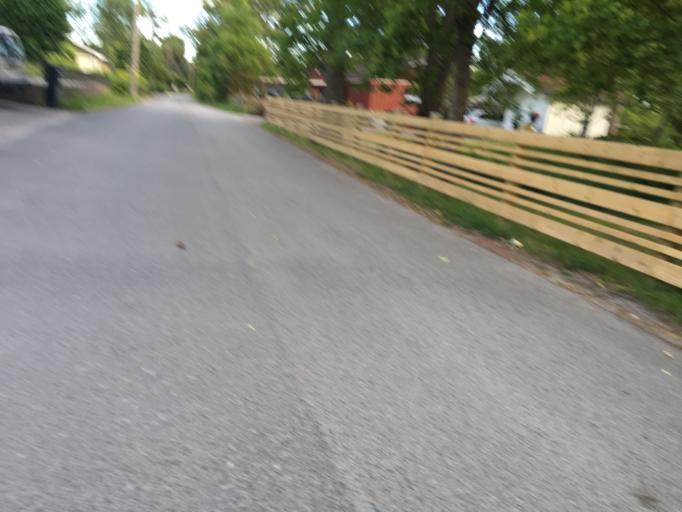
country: SE
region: Stockholm
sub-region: Nacka Kommun
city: Fisksatra
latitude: 59.3193
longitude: 18.2365
